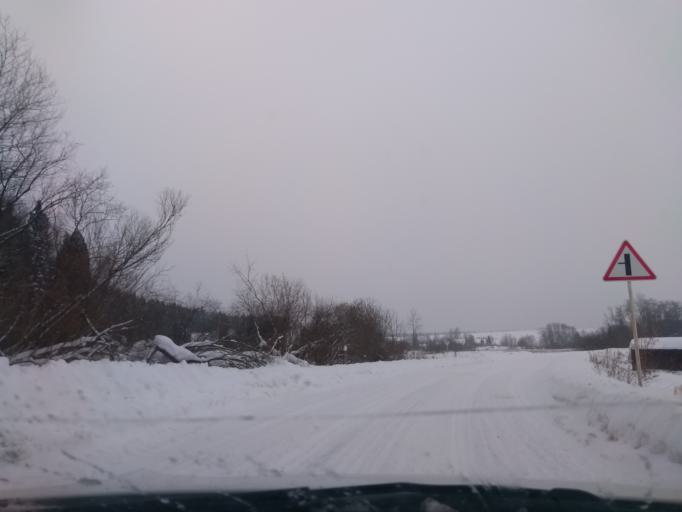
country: RU
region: Perm
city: Sylva
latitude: 57.8352
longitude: 56.7028
